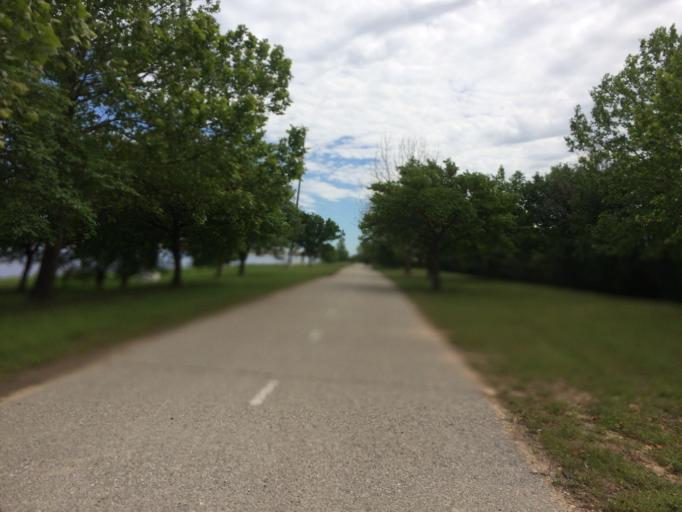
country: US
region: Oklahoma
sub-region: Oklahoma County
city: Oklahoma City
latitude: 35.4569
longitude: -97.4989
